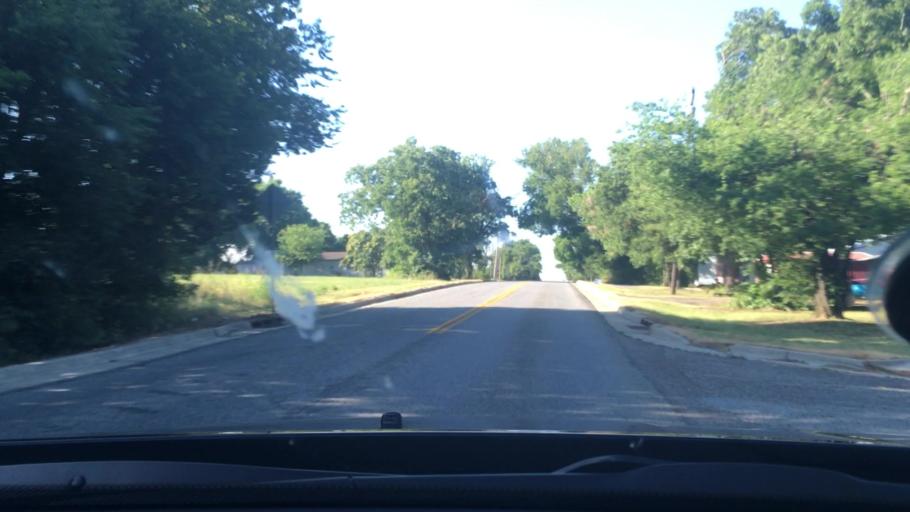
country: US
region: Oklahoma
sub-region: Murray County
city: Sulphur
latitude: 34.4022
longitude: -96.8271
